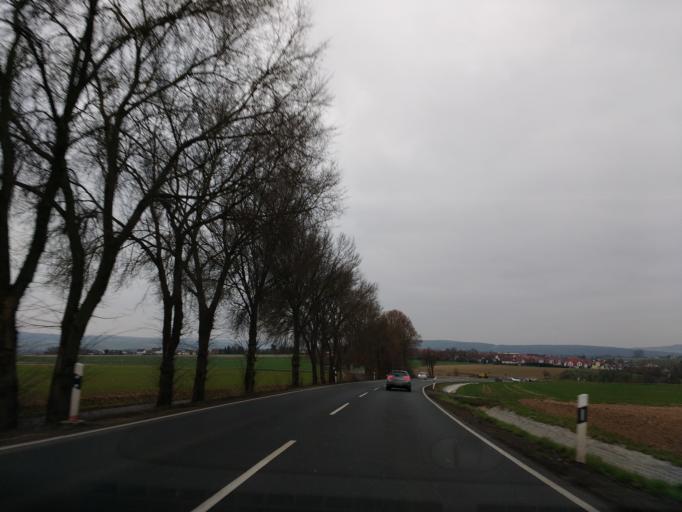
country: DE
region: Hesse
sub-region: Regierungsbezirk Kassel
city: Baunatal
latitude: 51.2224
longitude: 9.4341
